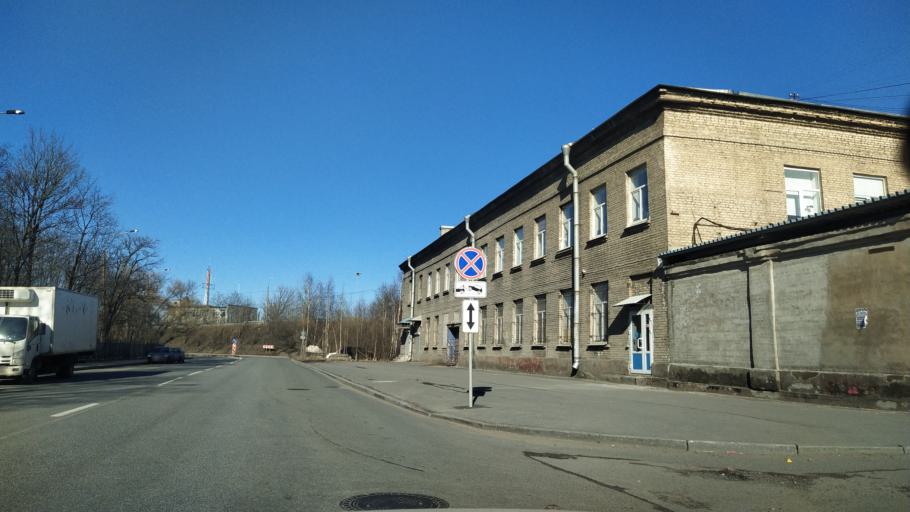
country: RU
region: St.-Petersburg
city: Centralniy
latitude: 59.9028
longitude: 30.3749
